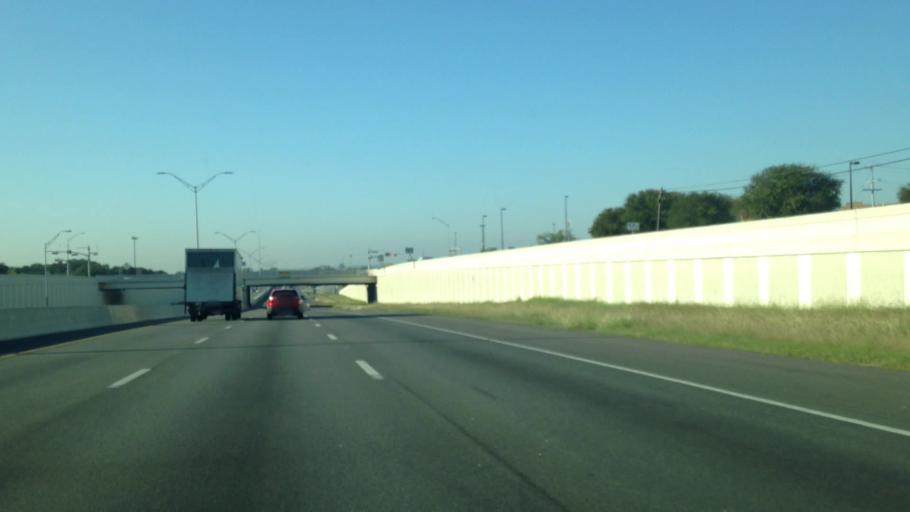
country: US
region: Texas
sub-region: Bexar County
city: Kirby
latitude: 29.4634
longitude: -98.4097
